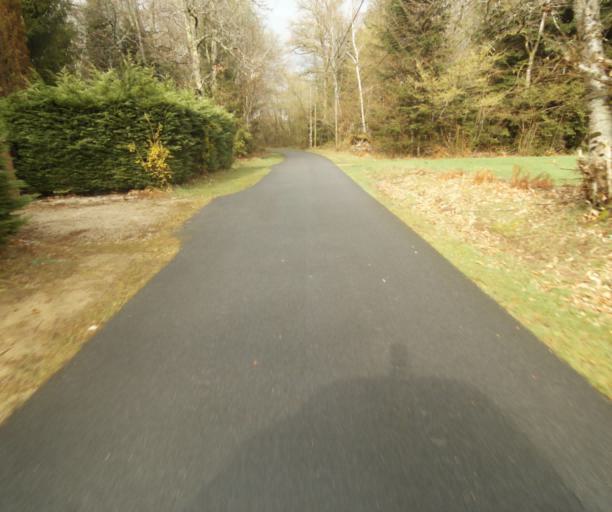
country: FR
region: Limousin
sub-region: Departement de la Correze
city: Saint-Privat
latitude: 45.2400
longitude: 2.0055
